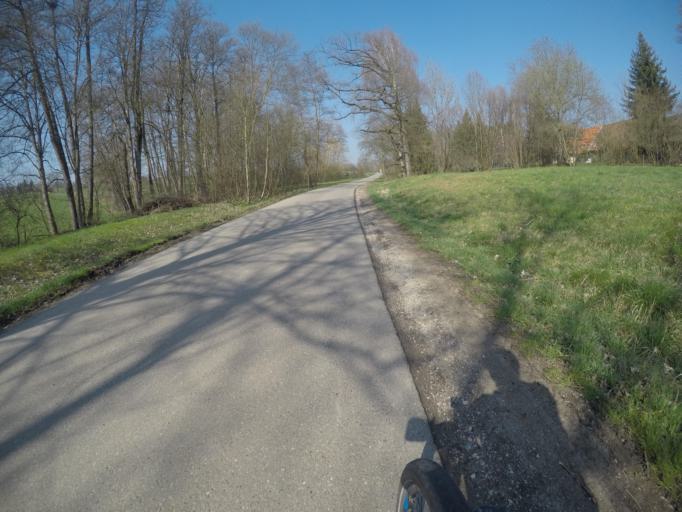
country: DE
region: Baden-Wuerttemberg
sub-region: Tuebingen Region
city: Pliezhausen
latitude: 48.5733
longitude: 9.2082
